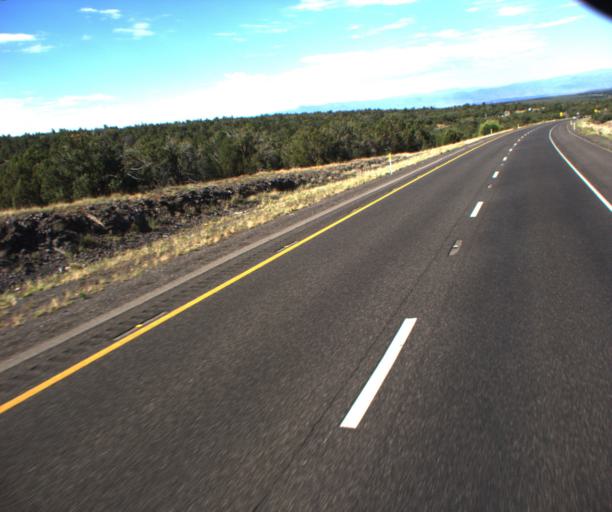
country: US
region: Arizona
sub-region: Yavapai County
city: Village of Oak Creek (Big Park)
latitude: 34.7846
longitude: -111.6097
